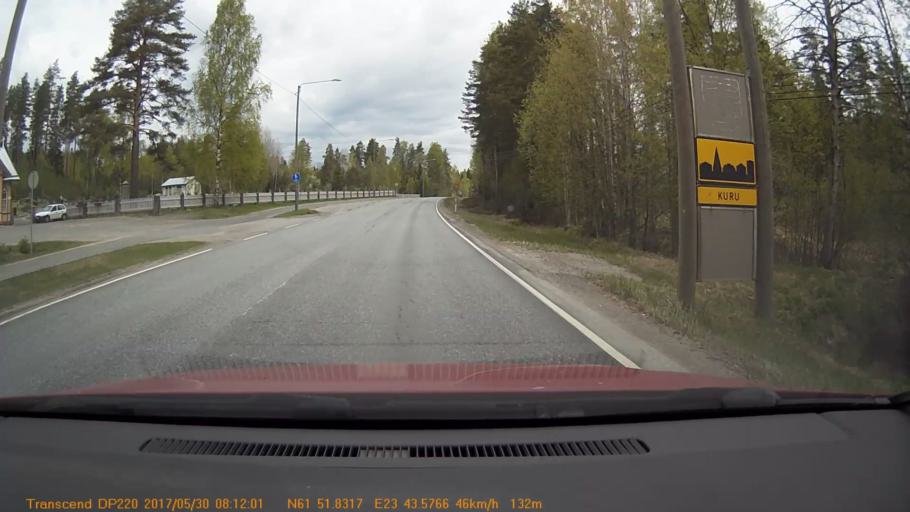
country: FI
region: Pirkanmaa
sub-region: Tampere
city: Kuru
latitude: 61.8636
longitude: 23.7263
